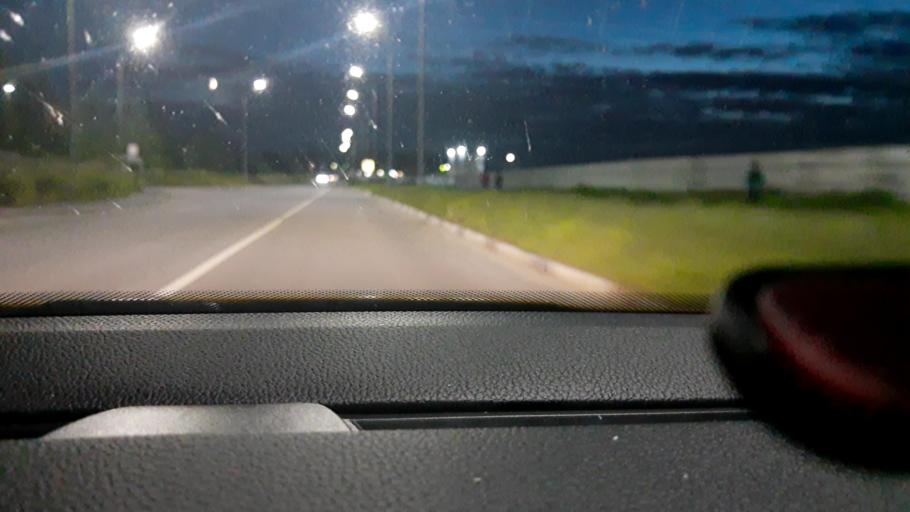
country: RU
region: Moskovskaya
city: Pirogovskiy
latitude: 55.9573
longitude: 37.6796
